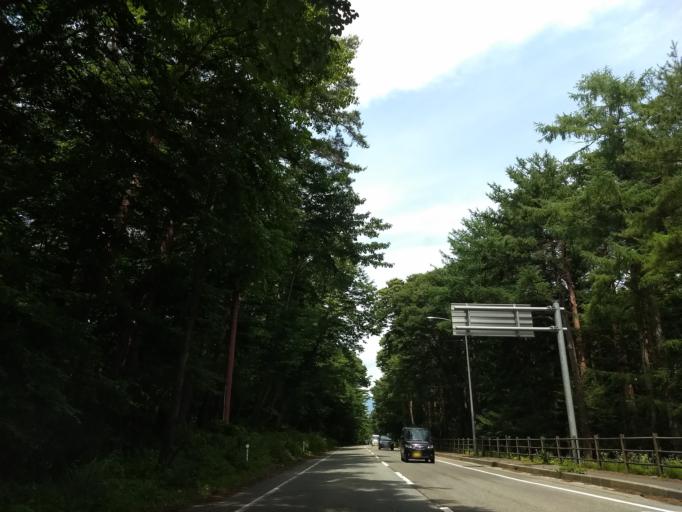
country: JP
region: Yamanashi
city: Fujikawaguchiko
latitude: 35.4479
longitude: 138.8195
